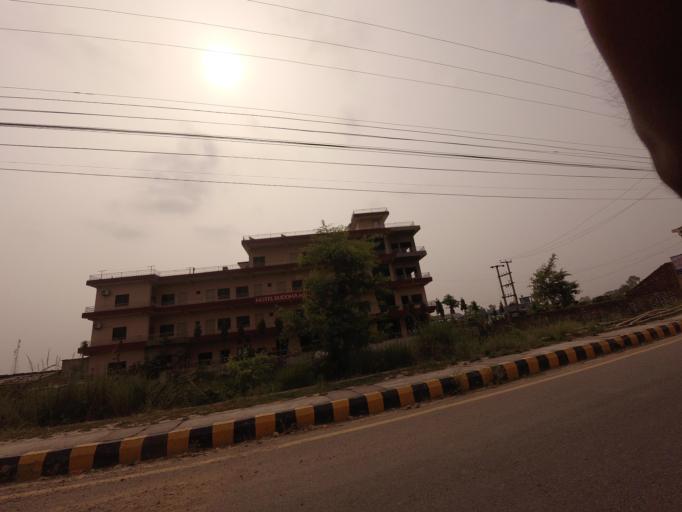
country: IN
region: Uttar Pradesh
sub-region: Maharajganj
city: Nautanwa
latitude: 27.4860
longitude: 83.2843
